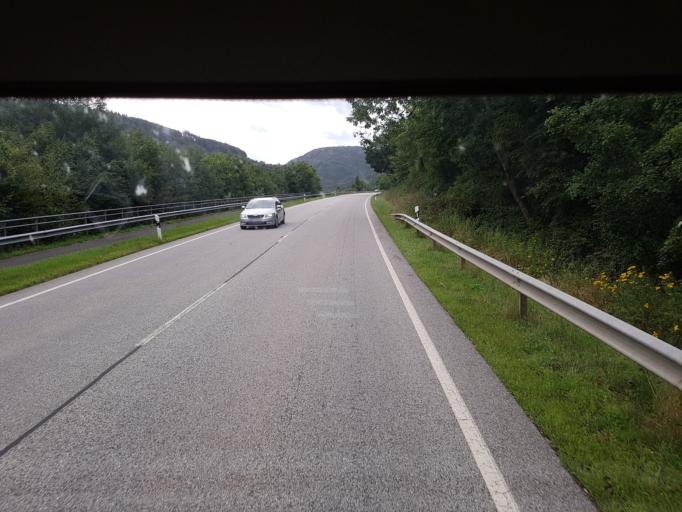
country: DE
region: Rheinland-Pfalz
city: Zell
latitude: 50.0291
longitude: 7.1753
